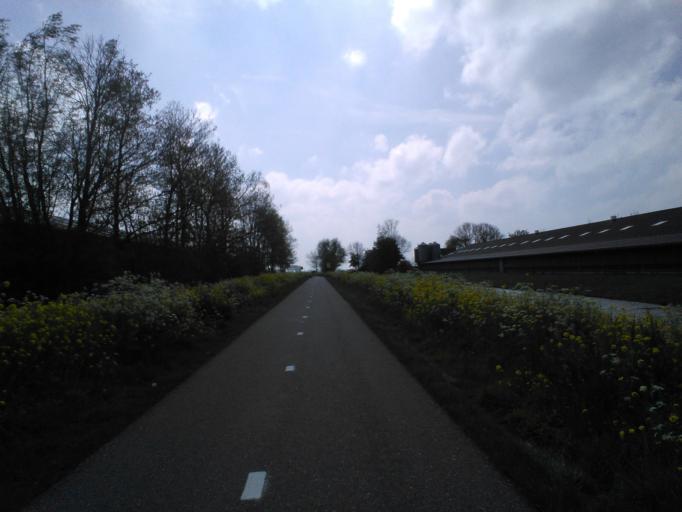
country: NL
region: South Holland
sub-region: Gemeente Leiderdorp
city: Leiderdorp
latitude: 52.1226
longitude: 4.5473
